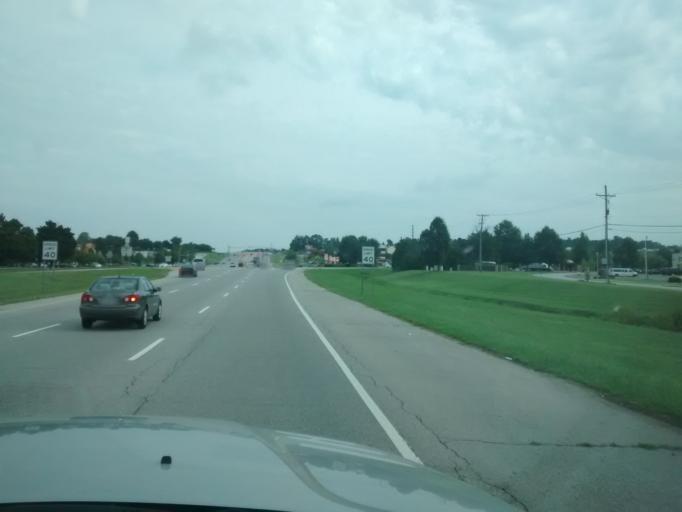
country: US
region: Arkansas
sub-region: Washington County
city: Johnson
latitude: 36.1205
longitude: -94.1448
